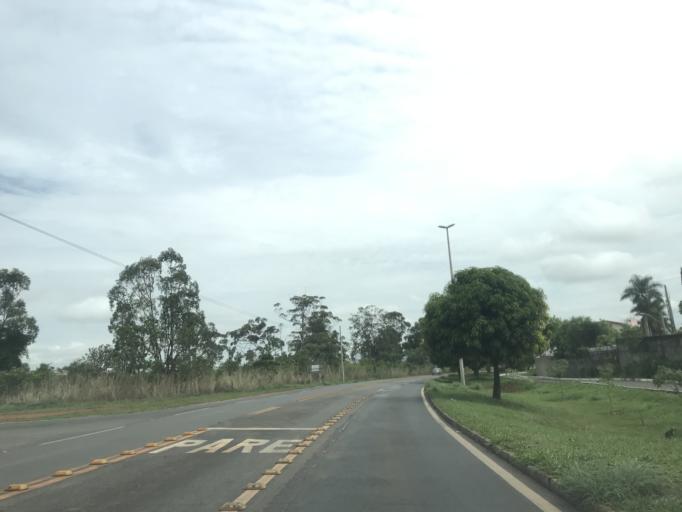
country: BR
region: Federal District
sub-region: Brasilia
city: Brasilia
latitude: -15.6857
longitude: -47.8376
